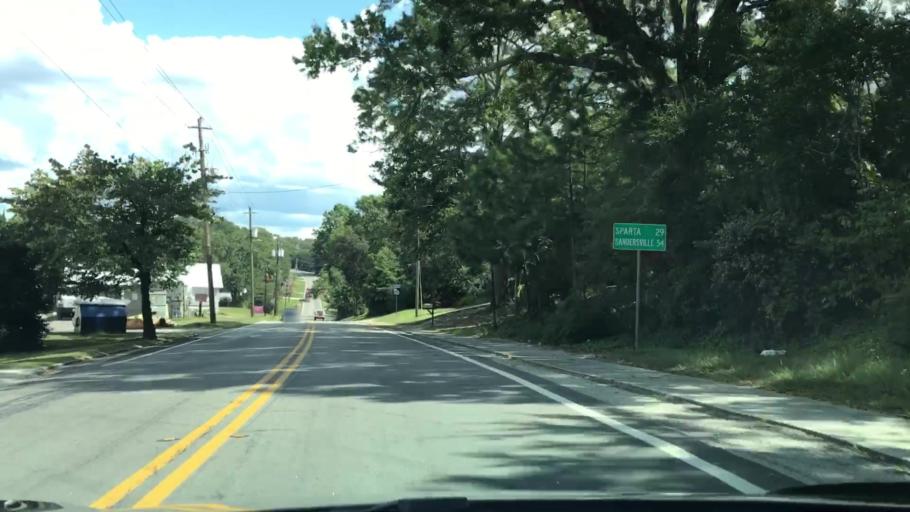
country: US
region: Georgia
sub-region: Greene County
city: Greensboro
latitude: 33.5750
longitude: -83.1779
